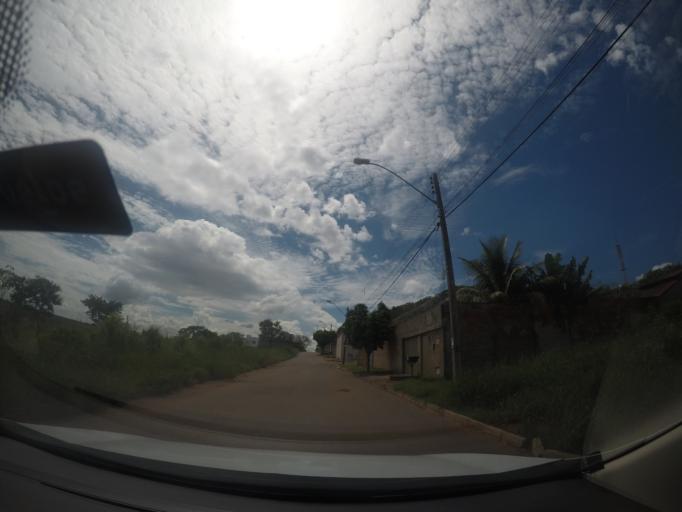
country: BR
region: Goias
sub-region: Goiania
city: Goiania
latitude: -16.6612
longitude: -49.3470
